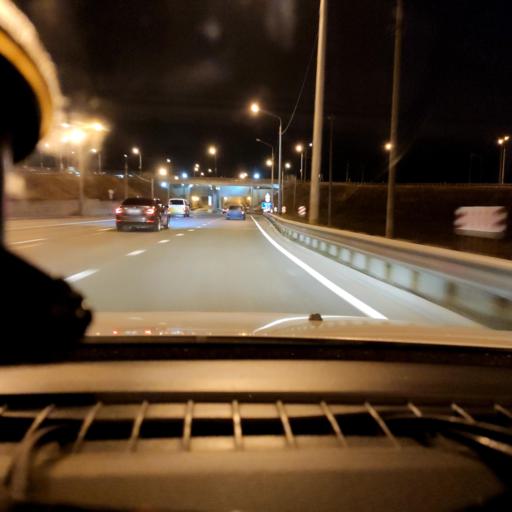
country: RU
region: Samara
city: Volzhskiy
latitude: 53.4354
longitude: 50.1133
